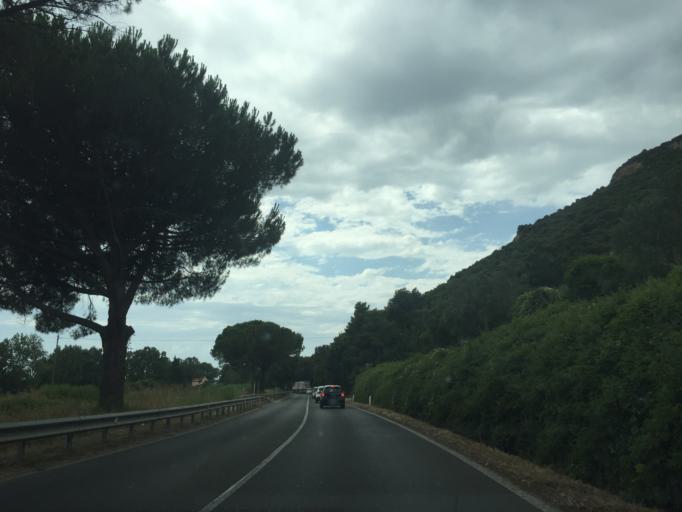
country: IT
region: Tuscany
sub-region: Province of Pisa
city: Asciano
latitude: 43.7525
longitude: 10.4507
